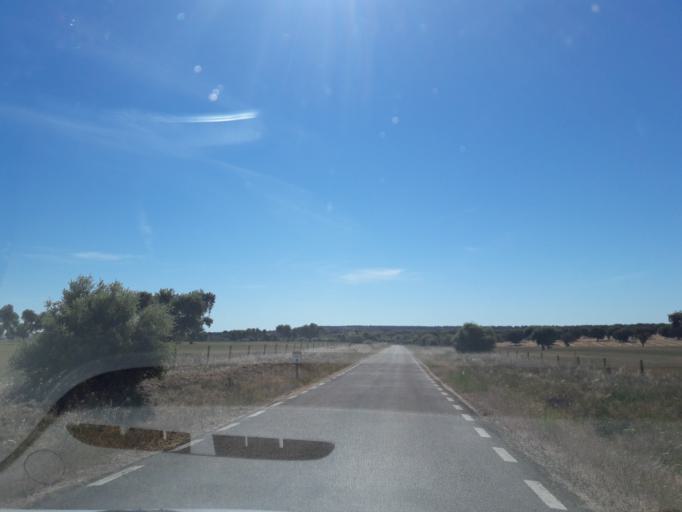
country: ES
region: Castille and Leon
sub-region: Provincia de Salamanca
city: Zarapicos
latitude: 41.0232
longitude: -5.8300
